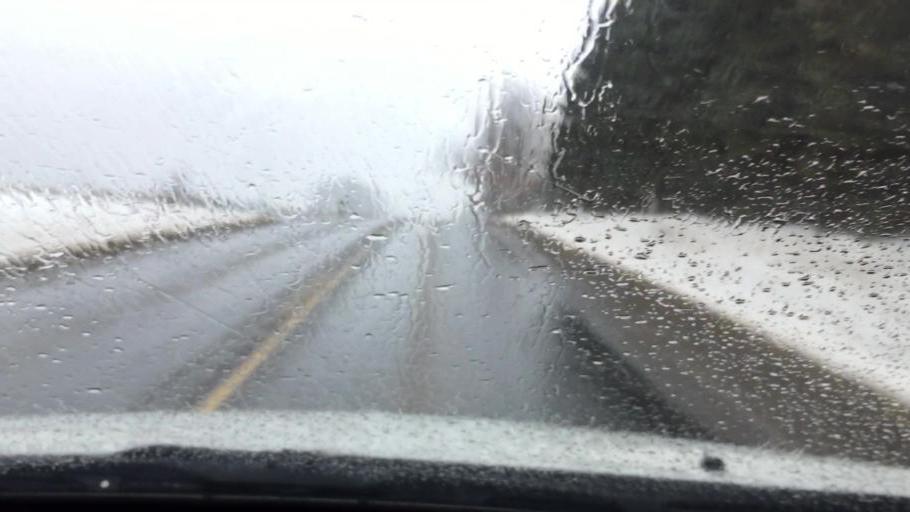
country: US
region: Michigan
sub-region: Osceola County
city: Reed City
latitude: 44.0334
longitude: -85.4439
